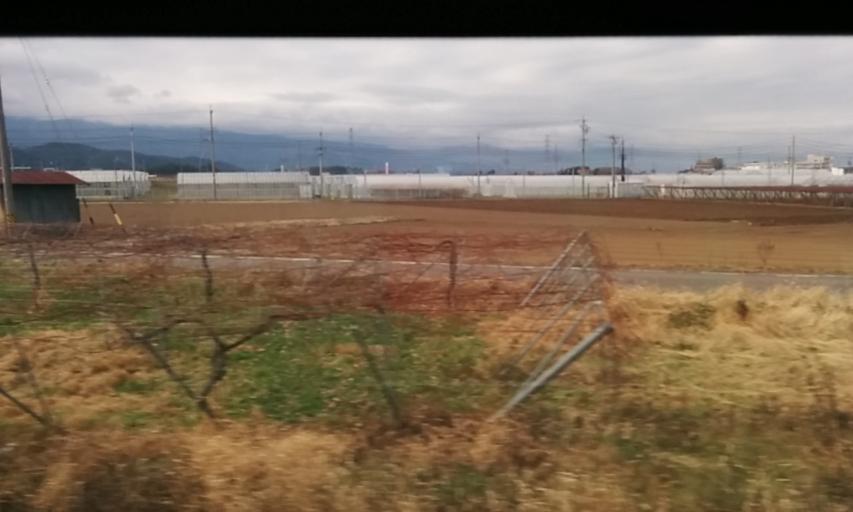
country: JP
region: Nagano
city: Shiojiri
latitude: 36.1037
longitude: 137.9363
